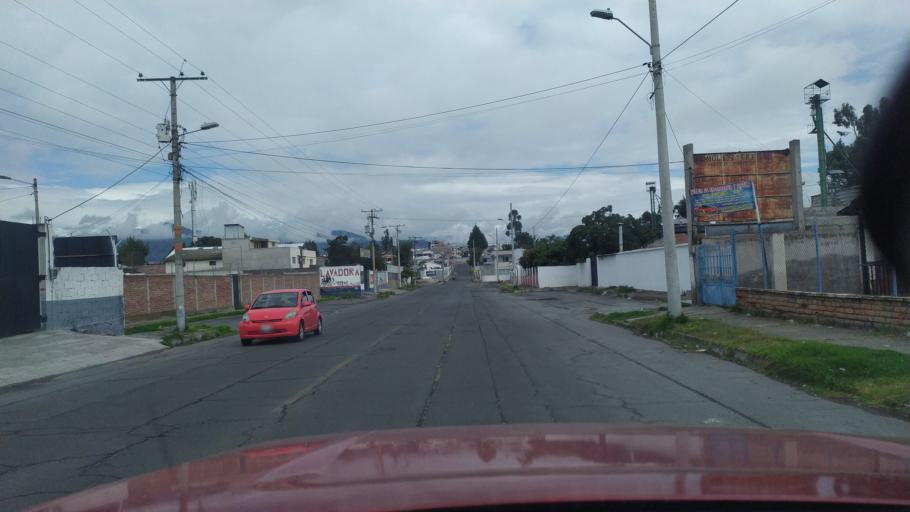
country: EC
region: Chimborazo
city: Riobamba
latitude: -1.6783
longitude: -78.6349
